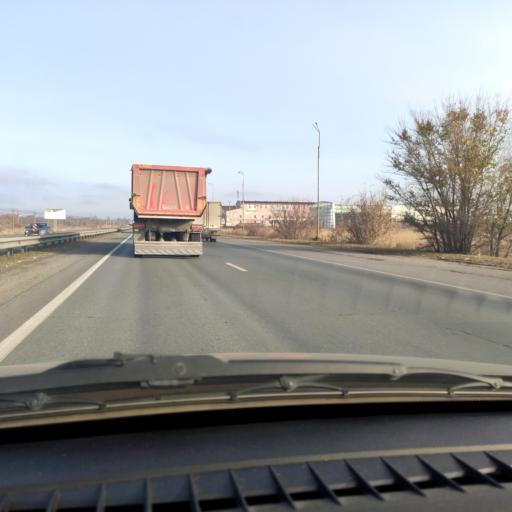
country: RU
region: Samara
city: Tol'yatti
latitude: 53.5700
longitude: 49.3832
